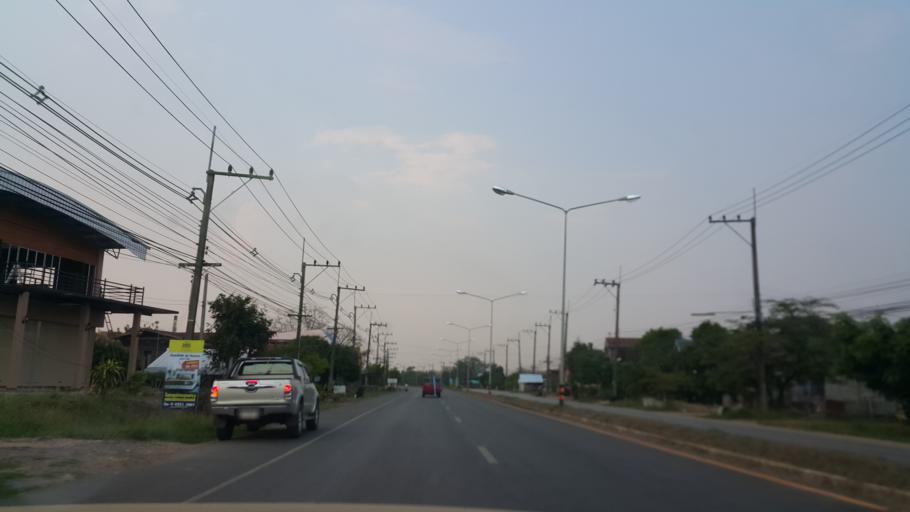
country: TH
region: Nakhon Phanom
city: That Phanom
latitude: 16.9863
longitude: 104.7271
